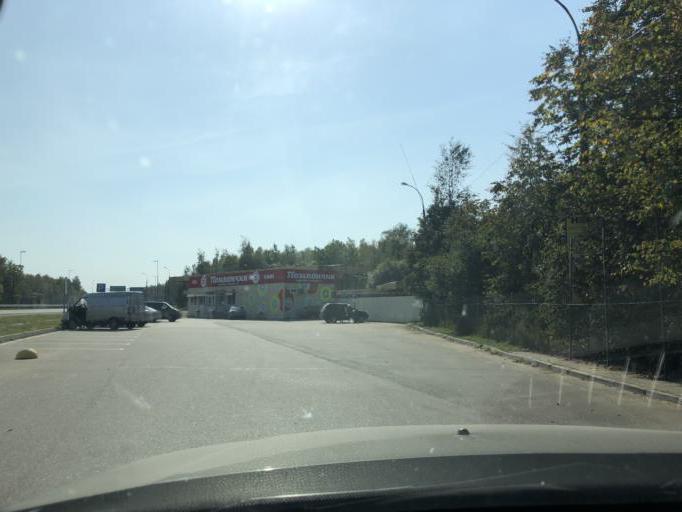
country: RU
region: Moskovskaya
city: Danki
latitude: 54.9224
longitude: 37.5169
